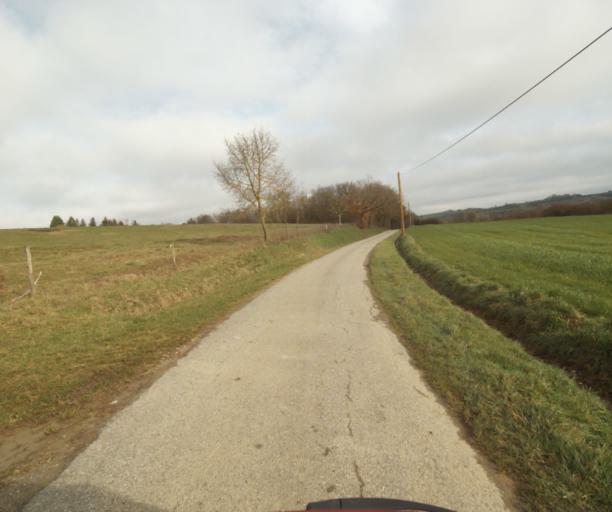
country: FR
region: Midi-Pyrenees
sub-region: Departement de la Haute-Garonne
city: Gaillac-Toulza
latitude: 43.1612
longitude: 1.4849
